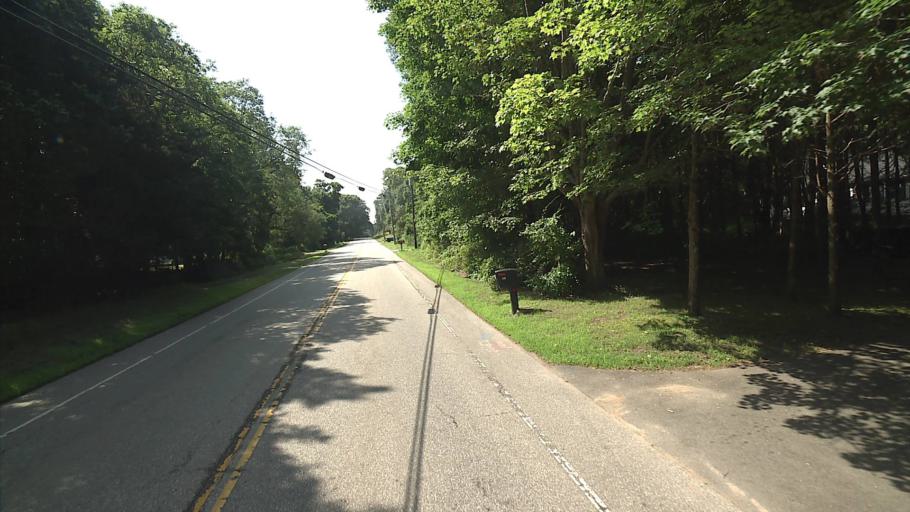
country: US
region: Connecticut
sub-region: Middlesex County
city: Clinton
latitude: 41.2830
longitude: -72.4881
